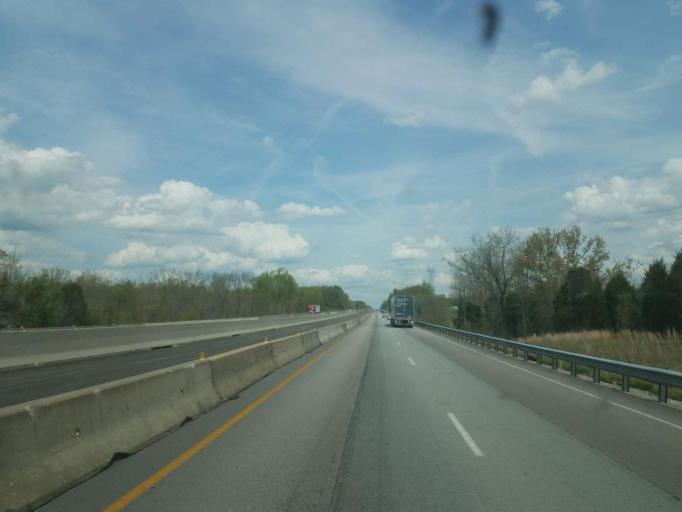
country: US
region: Kentucky
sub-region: Hardin County
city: Elizabethtown
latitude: 37.6255
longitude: -85.8622
